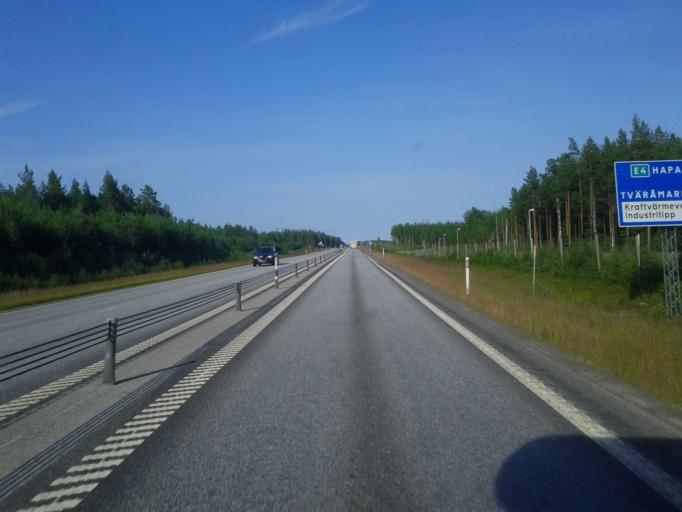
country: SE
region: Vaesterbotten
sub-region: Umea Kommun
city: Taftea
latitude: 63.8593
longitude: 20.4040
